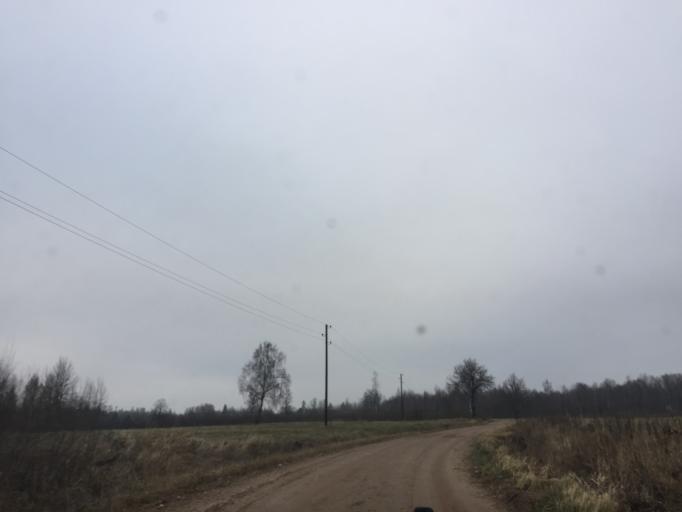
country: LV
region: Limbazu Rajons
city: Limbazi
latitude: 57.5762
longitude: 24.5476
